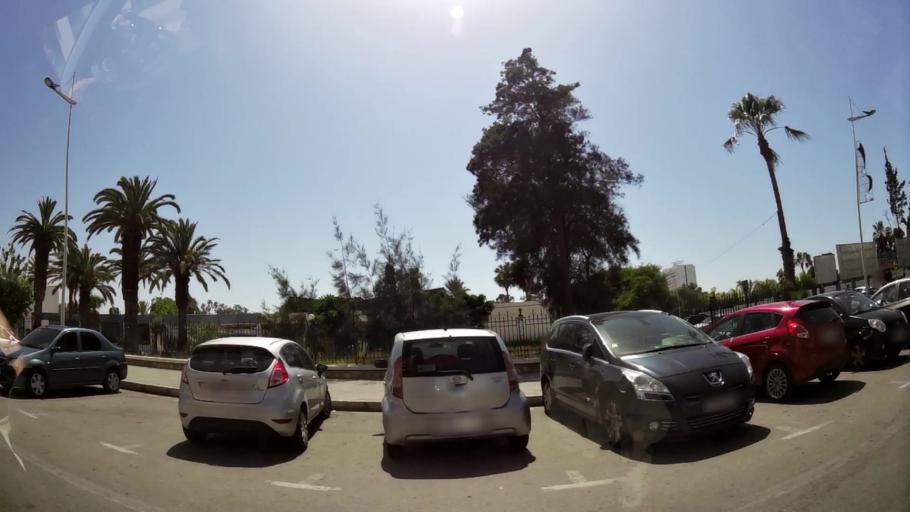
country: MA
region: Souss-Massa-Draa
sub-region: Agadir-Ida-ou-Tnan
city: Agadir
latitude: 30.4177
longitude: -9.5968
